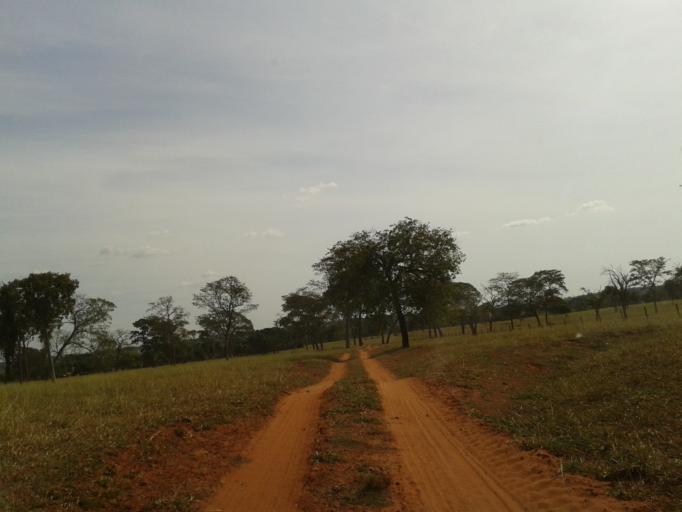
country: BR
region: Minas Gerais
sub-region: Campina Verde
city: Campina Verde
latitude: -19.5144
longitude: -49.5933
